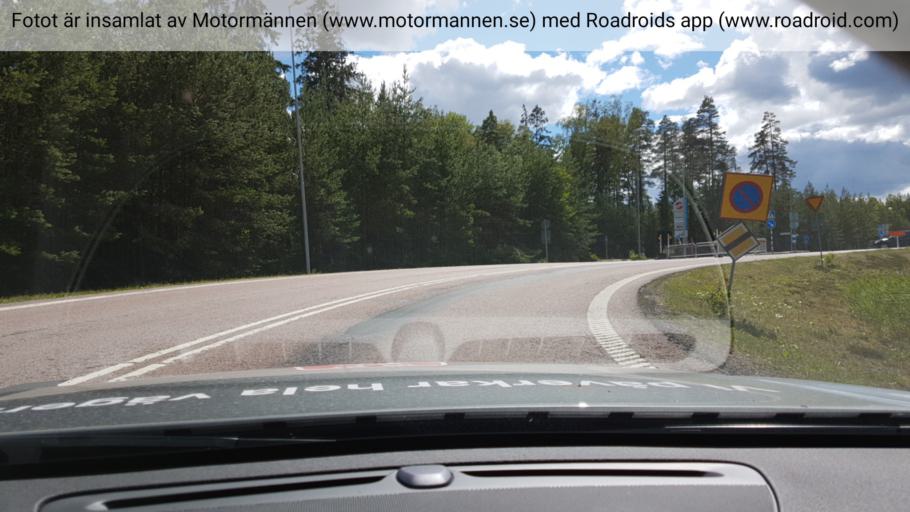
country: SE
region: Stockholm
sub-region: Sigtuna Kommun
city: Rosersberg
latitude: 59.6139
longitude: 17.8927
